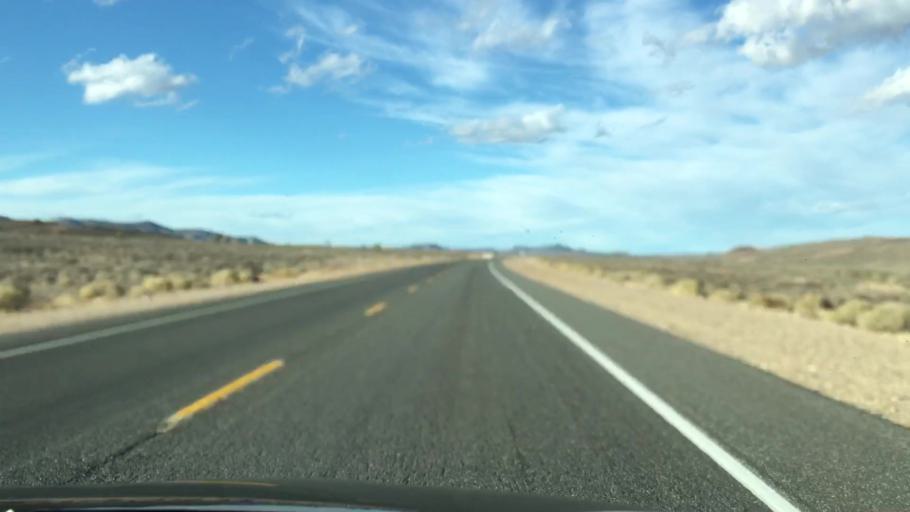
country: US
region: Nevada
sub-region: Esmeralda County
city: Goldfield
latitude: 37.5403
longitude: -117.1950
